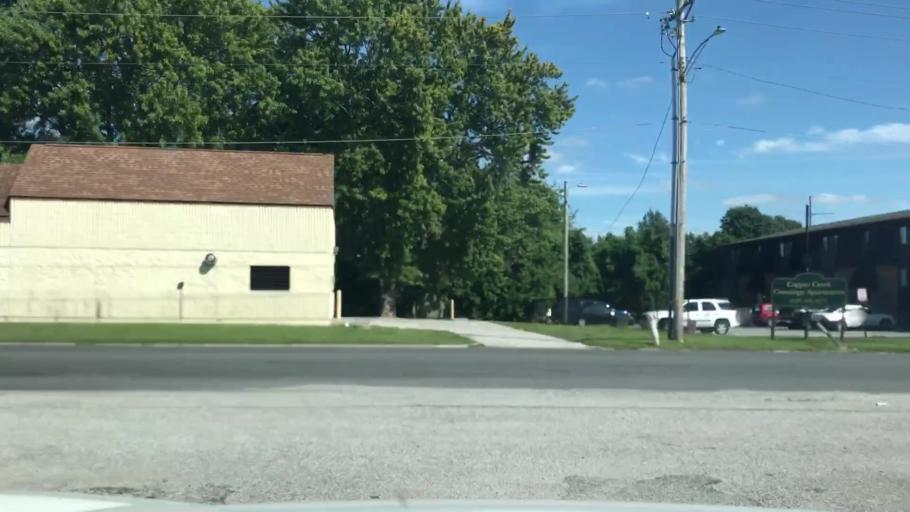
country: US
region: Illinois
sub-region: Saint Clair County
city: Swansea
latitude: 38.5410
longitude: -90.0299
